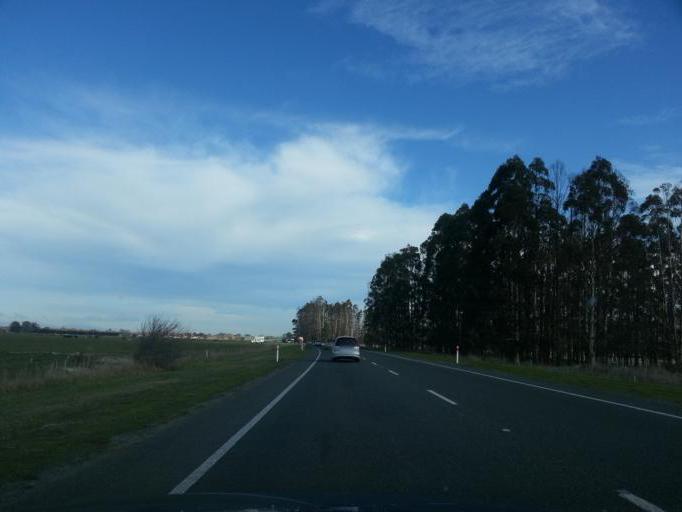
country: NZ
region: Canterbury
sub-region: Waimakariri District
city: Kaiapoi
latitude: -43.3606
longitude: 172.6532
